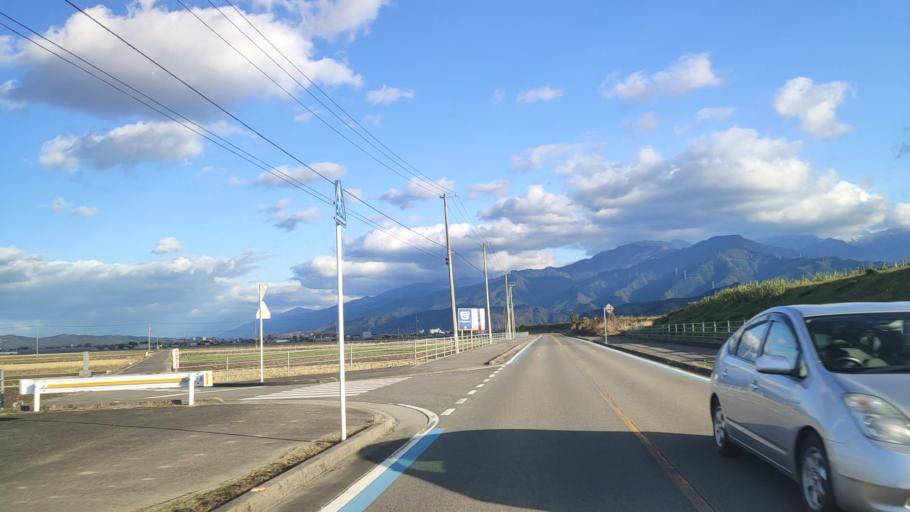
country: JP
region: Ehime
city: Saijo
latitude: 33.9102
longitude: 133.1356
